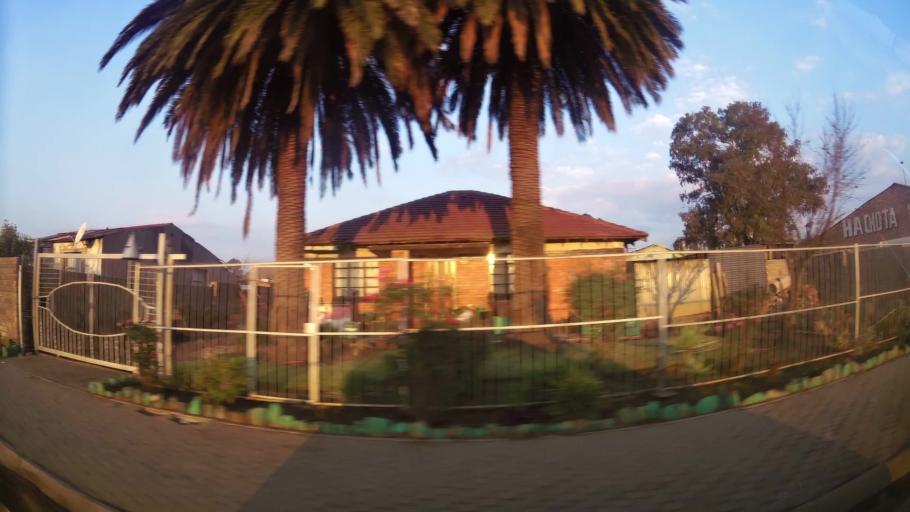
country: ZA
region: Gauteng
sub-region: City of Johannesburg Metropolitan Municipality
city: Orange Farm
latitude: -26.5410
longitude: 27.8821
